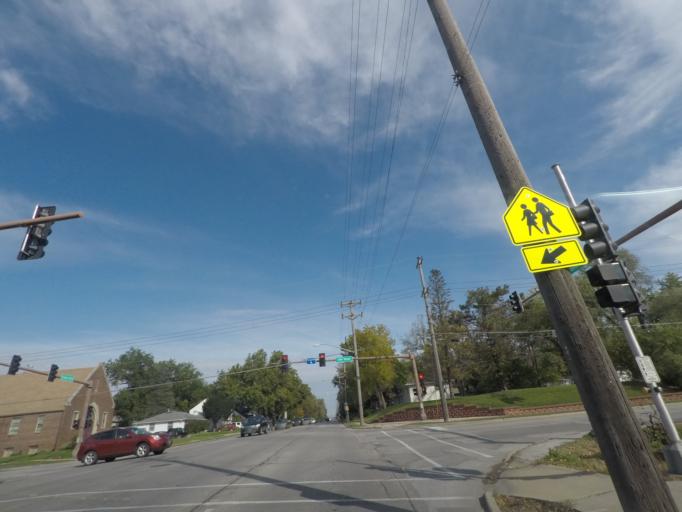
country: US
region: Iowa
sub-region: Story County
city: Ames
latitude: 42.0343
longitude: -93.6203
